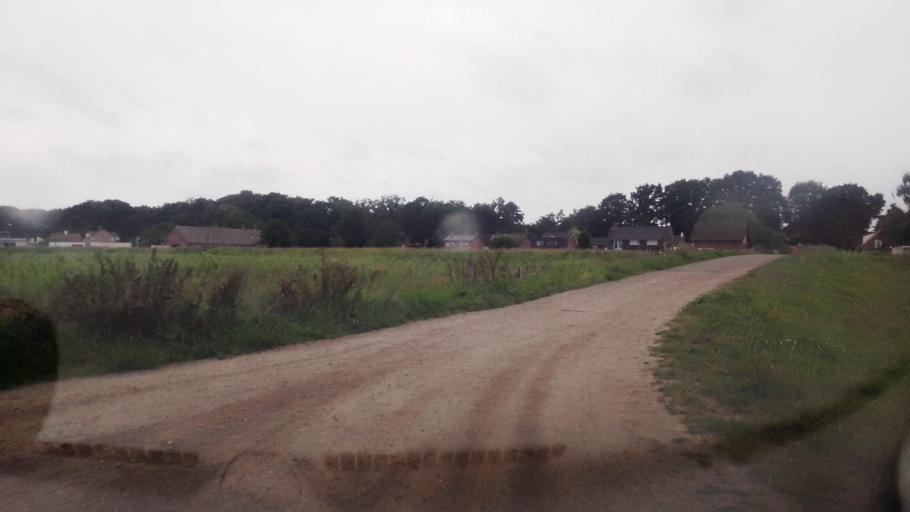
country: NL
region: Limburg
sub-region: Gemeente Venlo
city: Venlo
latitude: 51.4175
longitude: 6.1521
